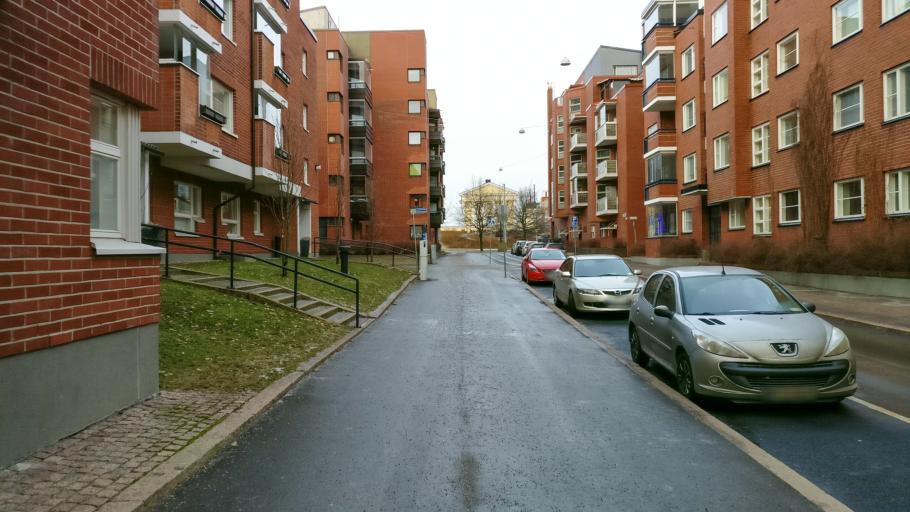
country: FI
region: Uusimaa
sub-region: Helsinki
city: Helsinki
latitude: 60.1666
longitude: 24.9755
